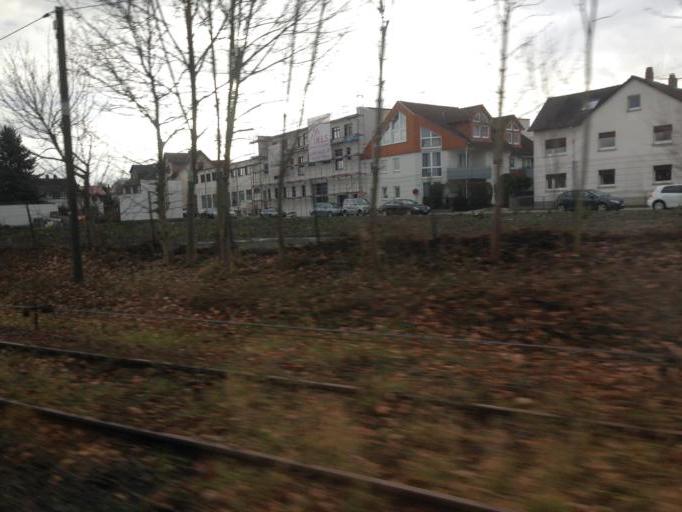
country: DE
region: Hesse
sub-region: Regierungsbezirk Giessen
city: Lich
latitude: 50.5152
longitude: 8.8203
